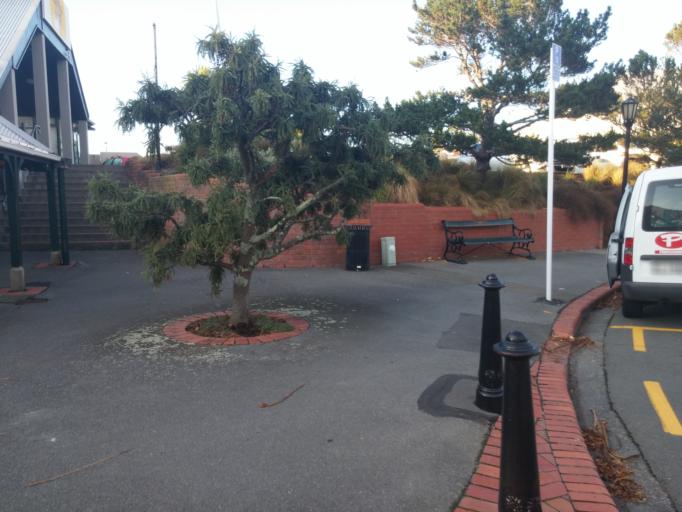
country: NZ
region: Wellington
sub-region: Wellington City
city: Kelburn
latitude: -41.2854
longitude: 174.7674
